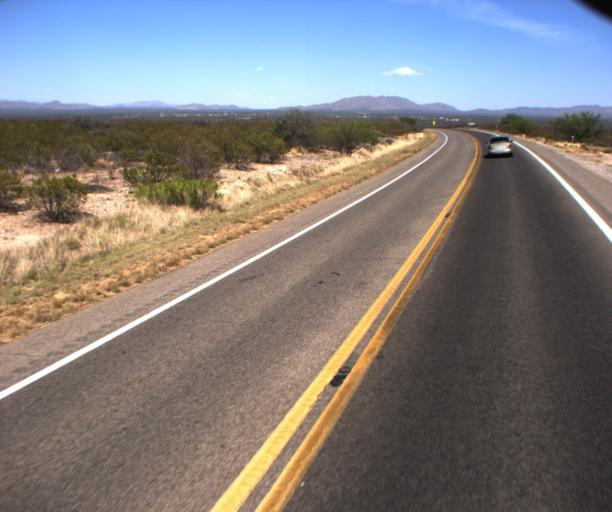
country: US
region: Arizona
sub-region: Cochise County
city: Sierra Vista Southeast
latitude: 31.5463
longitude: -110.1557
